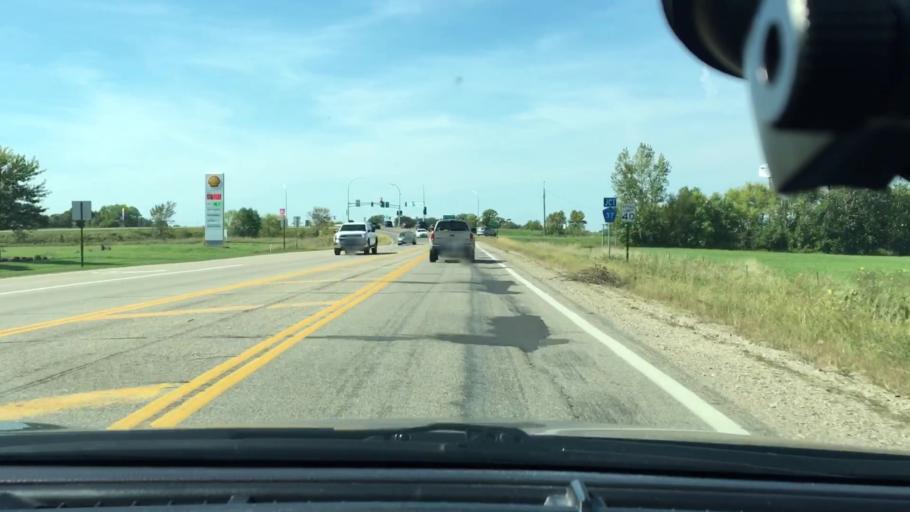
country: US
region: Minnesota
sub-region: Wright County
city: Albertville
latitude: 45.2381
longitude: -93.6444
